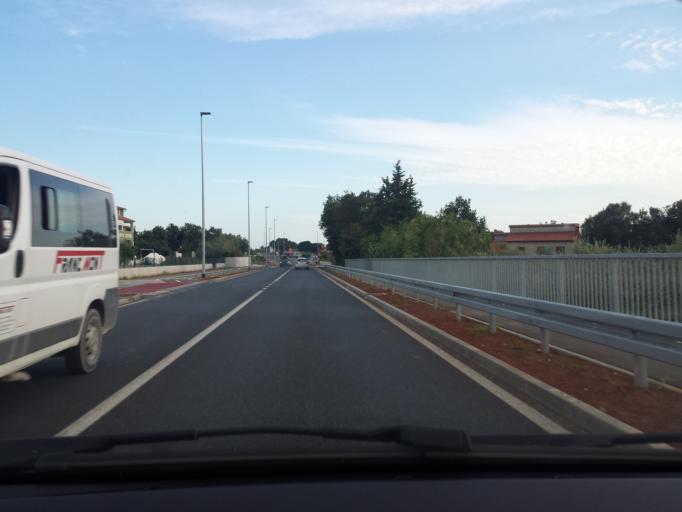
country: HR
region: Istarska
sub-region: Grad Pula
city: Pula
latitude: 44.9013
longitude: 13.8455
